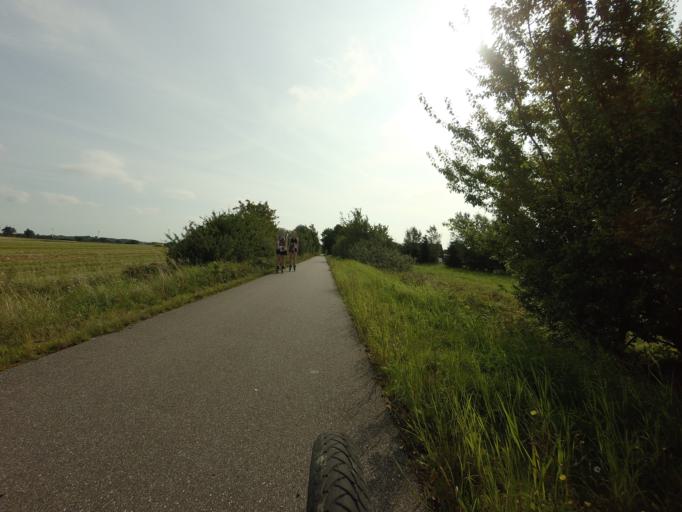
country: DK
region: Zealand
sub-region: Naestved Kommune
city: Fuglebjerg
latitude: 55.2630
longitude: 11.5465
